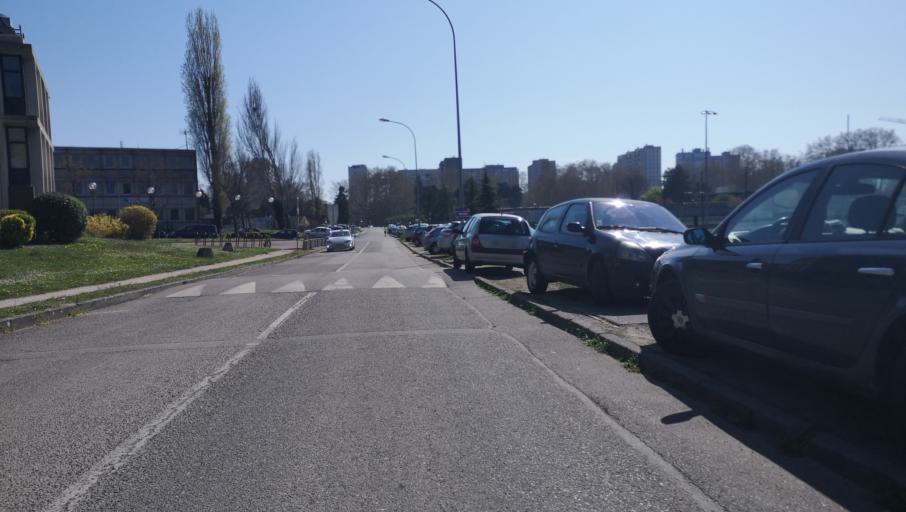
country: FR
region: Rhone-Alpes
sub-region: Departement du Rhone
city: Villeurbanne
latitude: 45.7831
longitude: 4.8649
